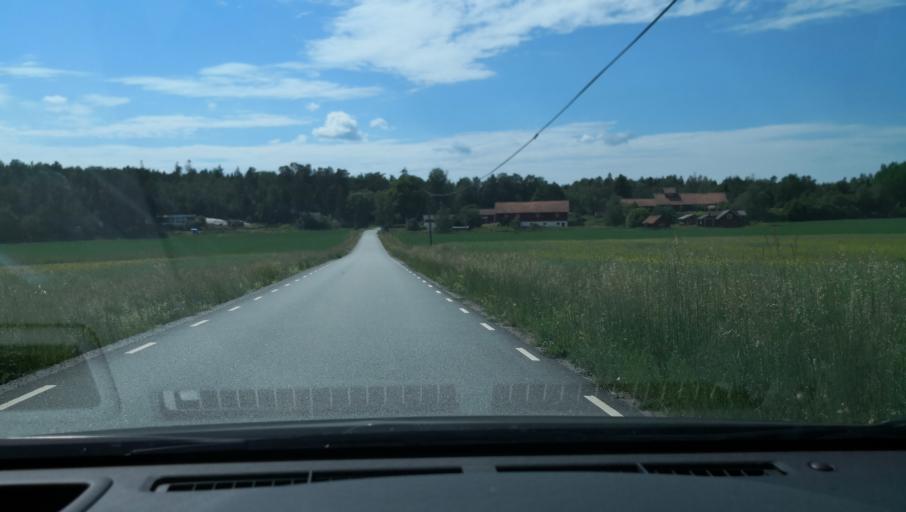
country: SE
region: Uppsala
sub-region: Habo Kommun
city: Balsta
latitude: 59.6700
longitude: 17.4606
